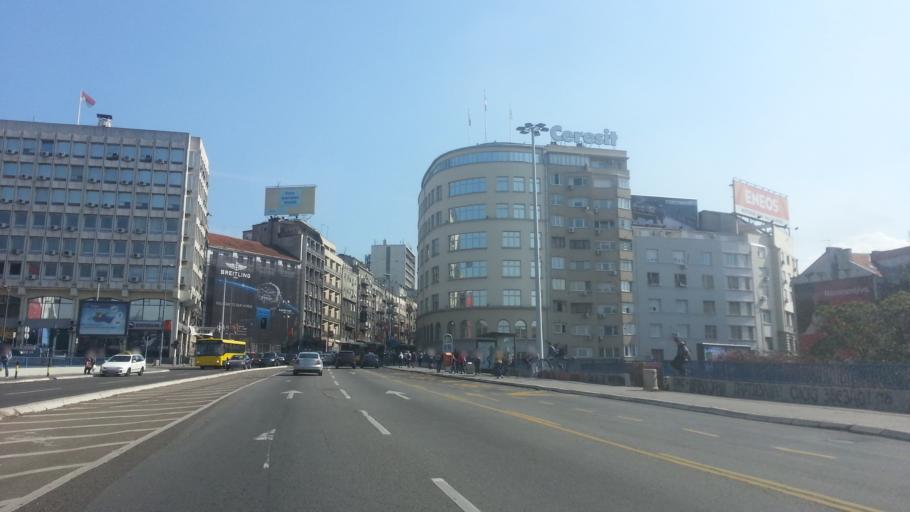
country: RS
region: Central Serbia
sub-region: Belgrade
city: Stari Grad
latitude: 44.8151
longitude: 20.4520
